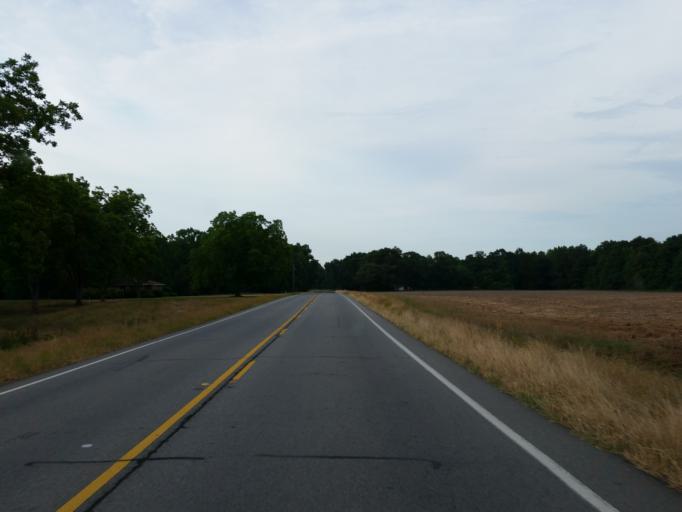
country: US
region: Georgia
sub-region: Dooly County
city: Unadilla
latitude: 32.2199
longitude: -83.7588
